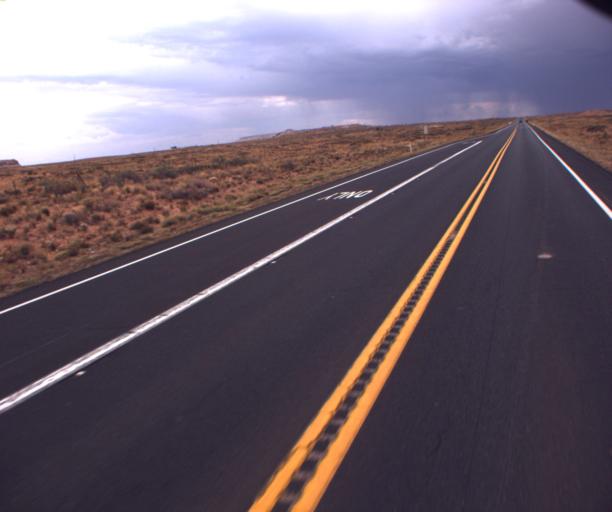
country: US
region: Arizona
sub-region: Coconino County
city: Kaibito
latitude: 36.3057
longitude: -110.9689
